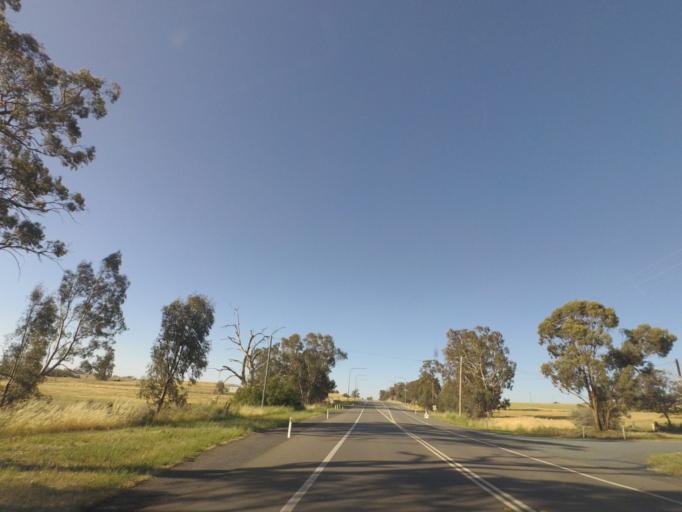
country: AU
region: New South Wales
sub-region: Wagga Wagga
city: Forest Hill
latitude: -35.2691
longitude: 147.7452
